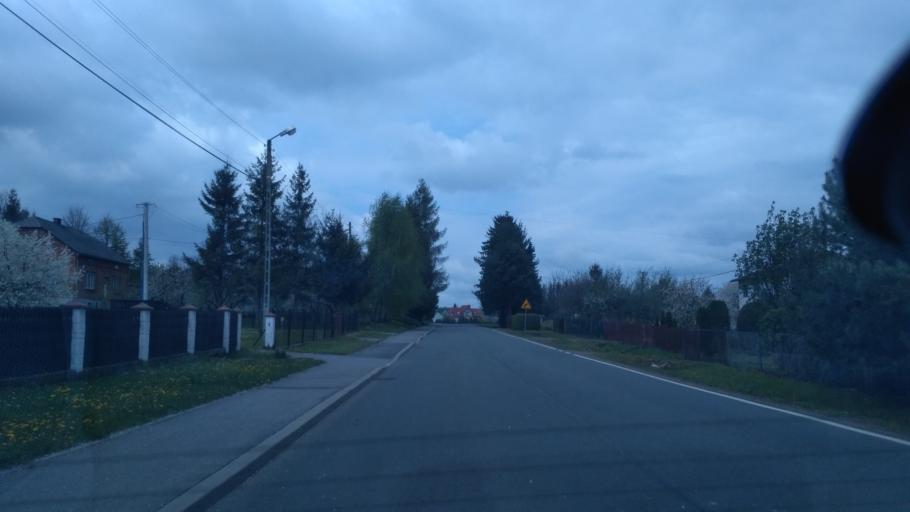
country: PL
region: Subcarpathian Voivodeship
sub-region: Powiat brzozowski
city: Jasionow
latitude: 49.6492
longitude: 21.9770
